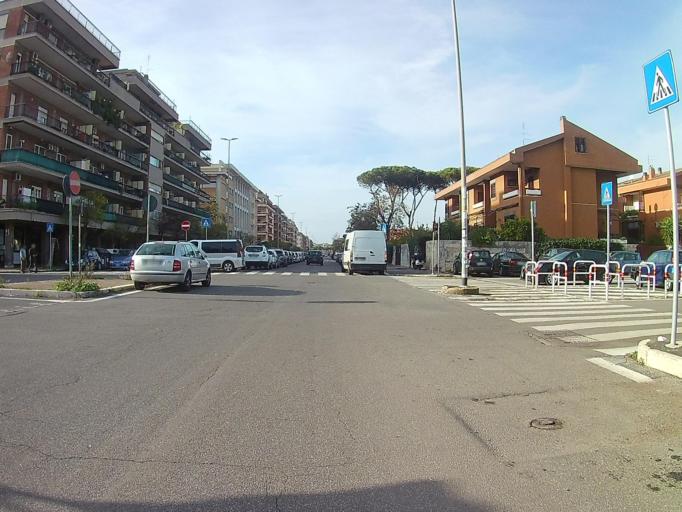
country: IT
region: Latium
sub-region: Citta metropolitana di Roma Capitale
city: Lido di Ostia
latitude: 41.7373
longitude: 12.2925
